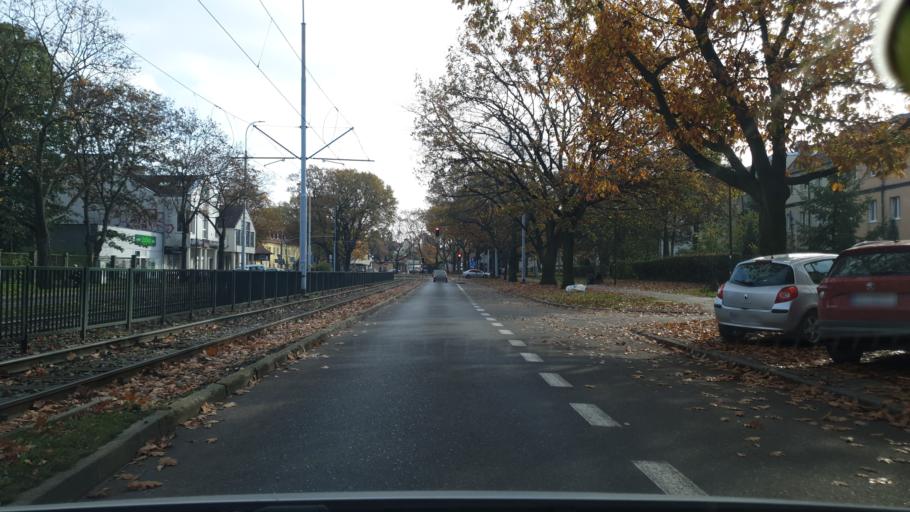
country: PL
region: Pomeranian Voivodeship
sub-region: Sopot
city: Sopot
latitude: 54.3880
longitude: 18.5821
